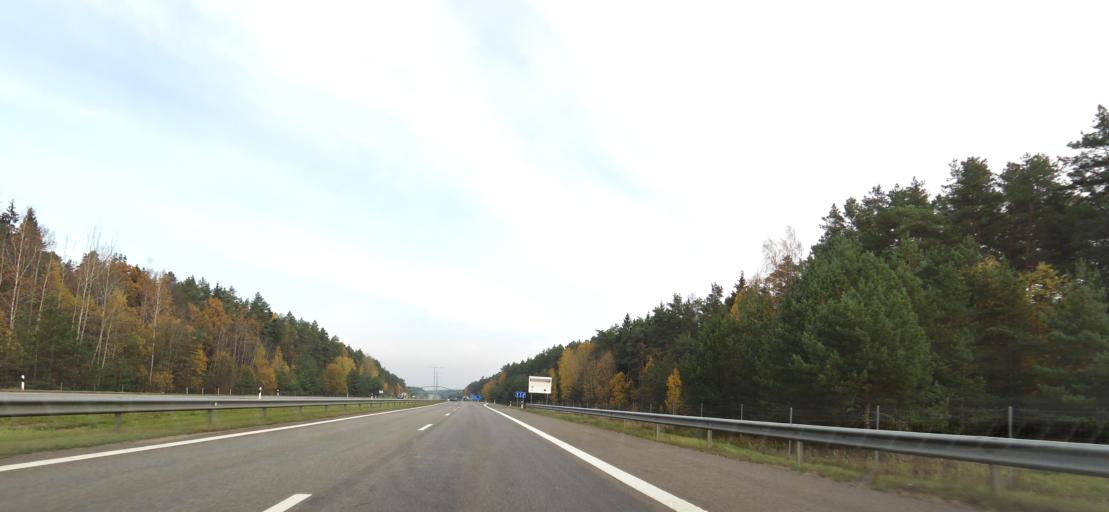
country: LT
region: Vilnius County
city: Ukmerge
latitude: 55.2420
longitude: 24.8208
